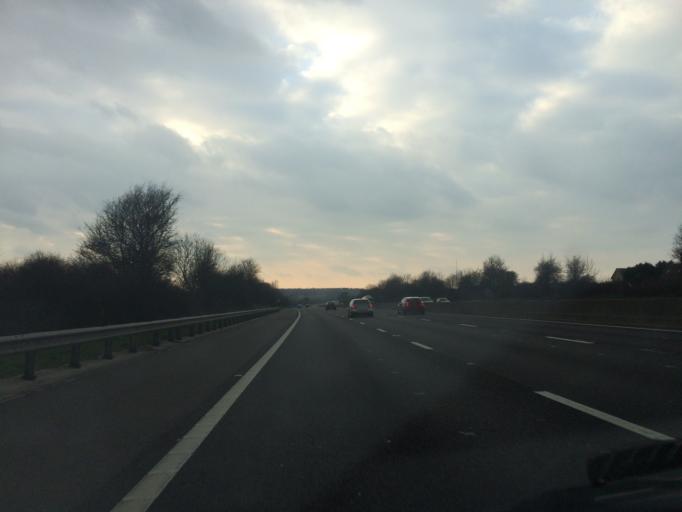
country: GB
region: England
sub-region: West Berkshire
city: Lambourn
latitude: 51.4703
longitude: -1.5231
